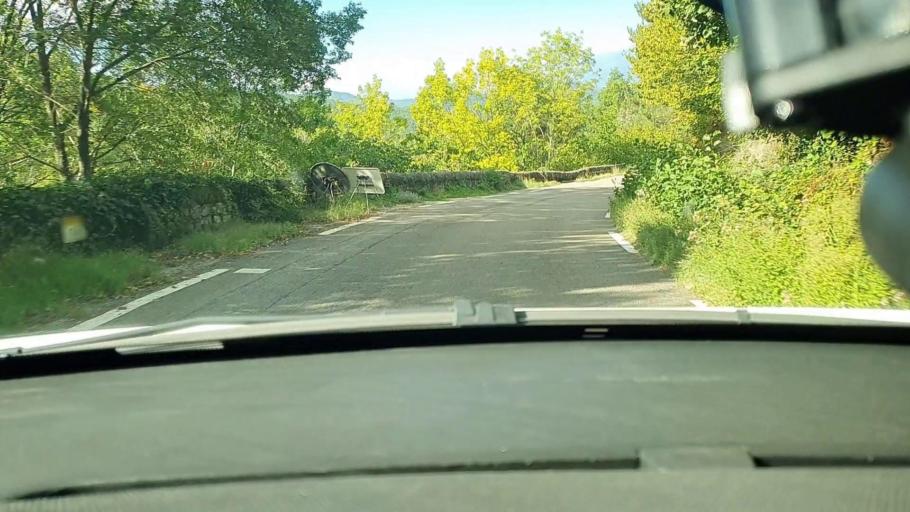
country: FR
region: Languedoc-Roussillon
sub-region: Departement du Gard
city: Besseges
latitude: 44.3592
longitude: 4.0127
